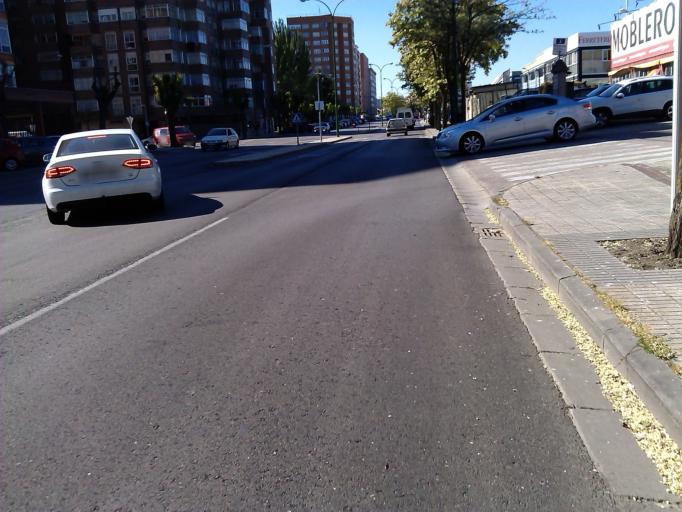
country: ES
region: Castille and Leon
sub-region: Provincia de Burgos
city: Burgos
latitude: 42.3514
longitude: -3.6609
